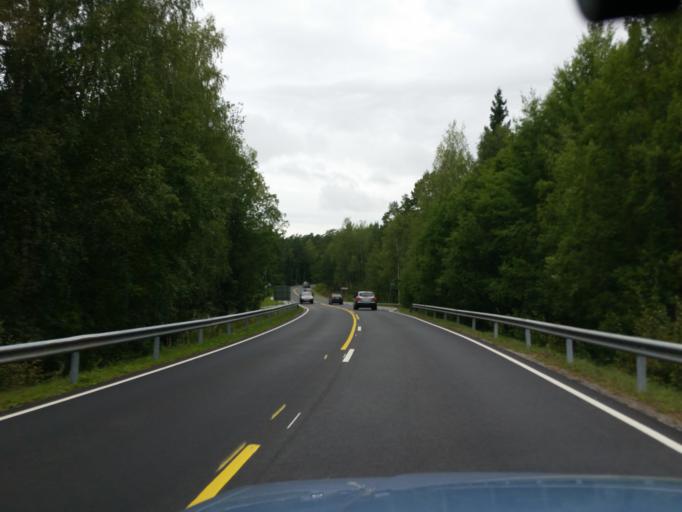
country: FI
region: Varsinais-Suomi
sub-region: Aboland-Turunmaa
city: Laensi-Turunmaa
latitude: 60.2524
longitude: 22.2384
